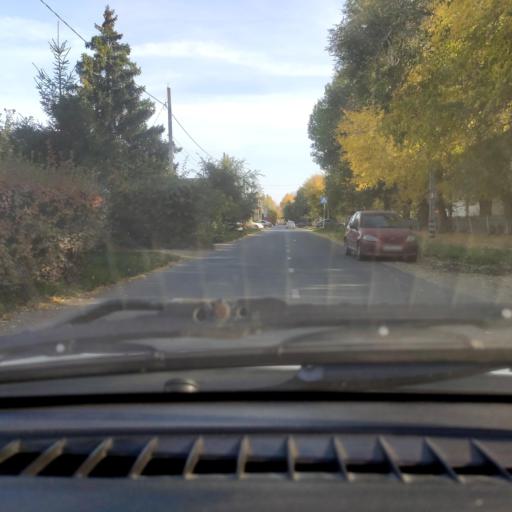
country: RU
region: Samara
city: Tol'yatti
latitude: 53.5087
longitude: 49.3996
